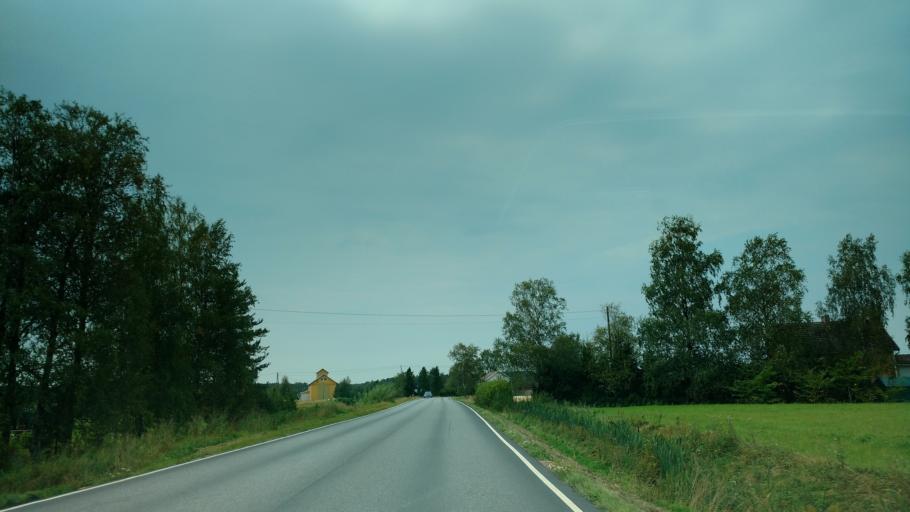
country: FI
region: Varsinais-Suomi
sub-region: Loimaa
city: Koski Tl
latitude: 60.6441
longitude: 23.1149
